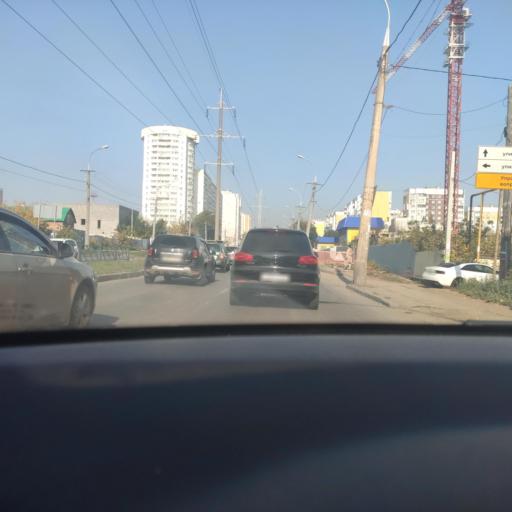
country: RU
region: Samara
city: Samara
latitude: 53.2044
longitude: 50.2139
